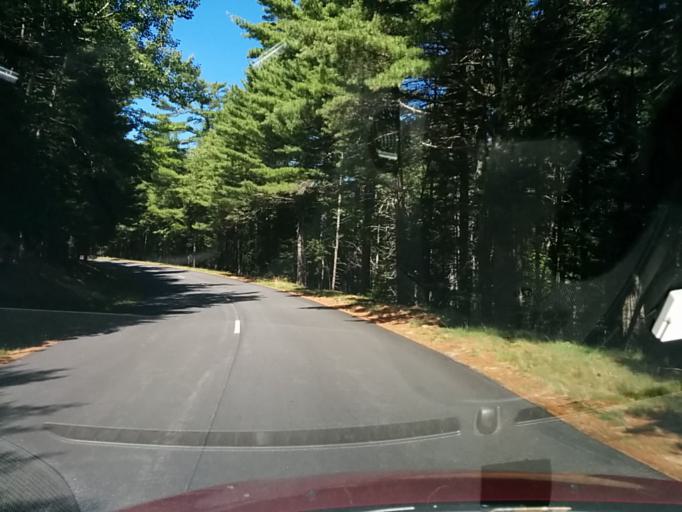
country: US
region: Maine
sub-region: Hancock County
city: Bar Harbor
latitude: 44.3171
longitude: -68.2276
